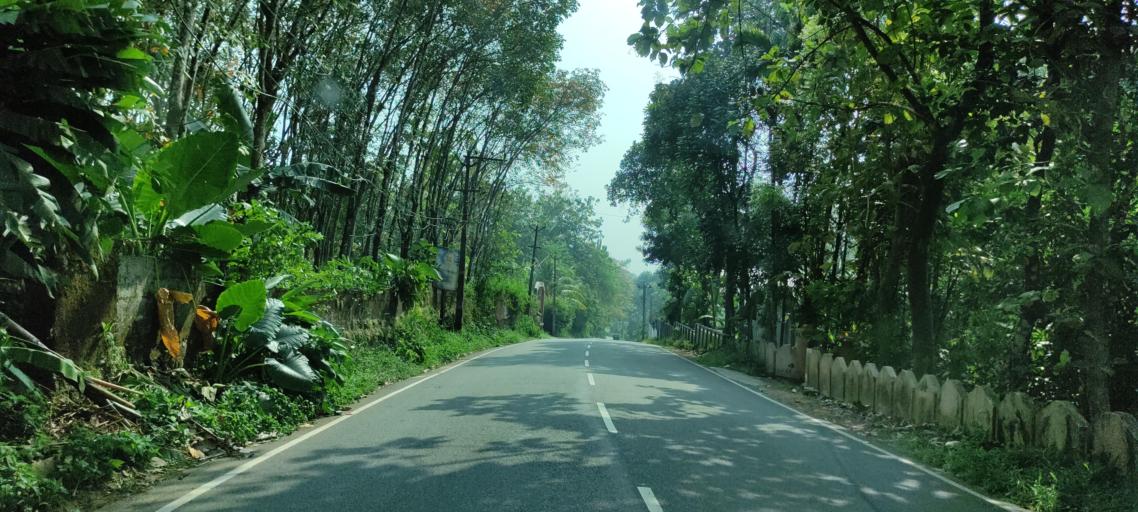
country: IN
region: Kerala
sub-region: Pattanamtitta
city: Pathanamthitta
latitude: 9.2213
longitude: 76.7498
